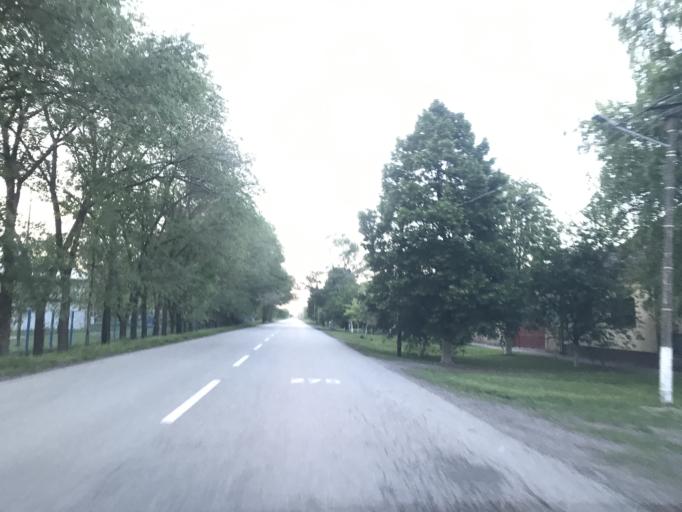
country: RS
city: Srpska Crnja
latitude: 45.7341
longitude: 20.6985
